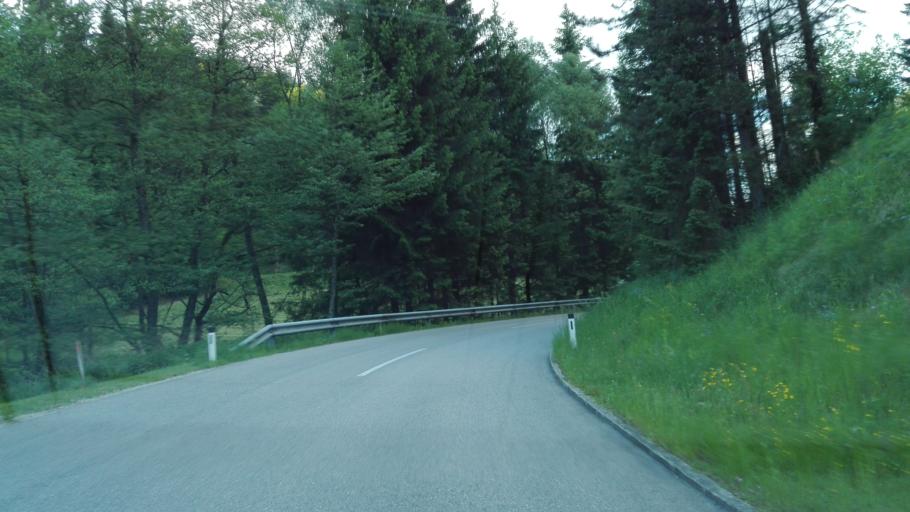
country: AT
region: Upper Austria
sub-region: Politischer Bezirk Freistadt
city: Freistadt
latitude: 48.4212
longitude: 14.6376
